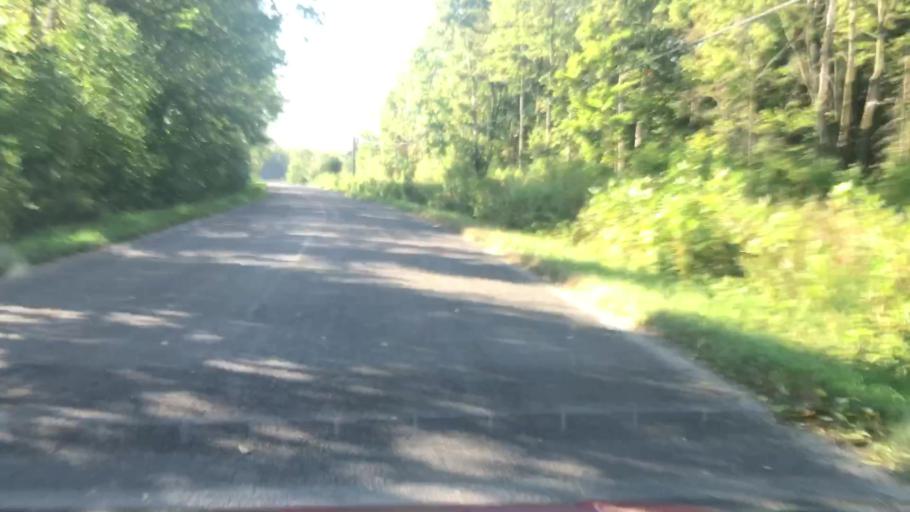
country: US
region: Michigan
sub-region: Chippewa County
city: Sault Ste. Marie
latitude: 46.2929
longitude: -84.0684
